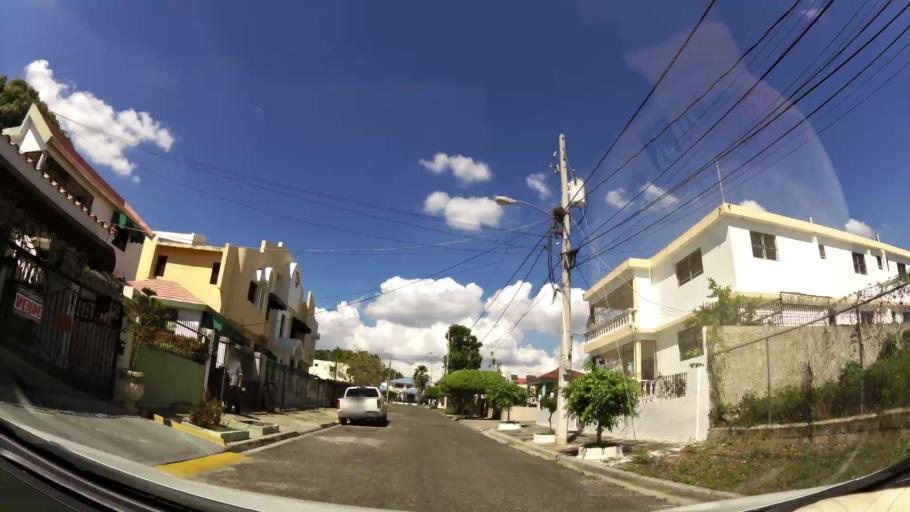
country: DO
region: Santiago
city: Santiago de los Caballeros
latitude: 19.4430
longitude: -70.6918
